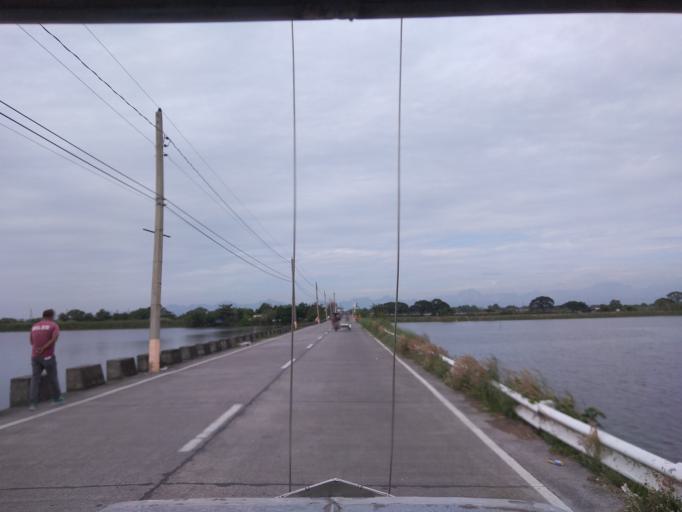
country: PH
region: Central Luzon
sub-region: Province of Pampanga
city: Lubao
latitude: 14.9378
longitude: 120.6116
